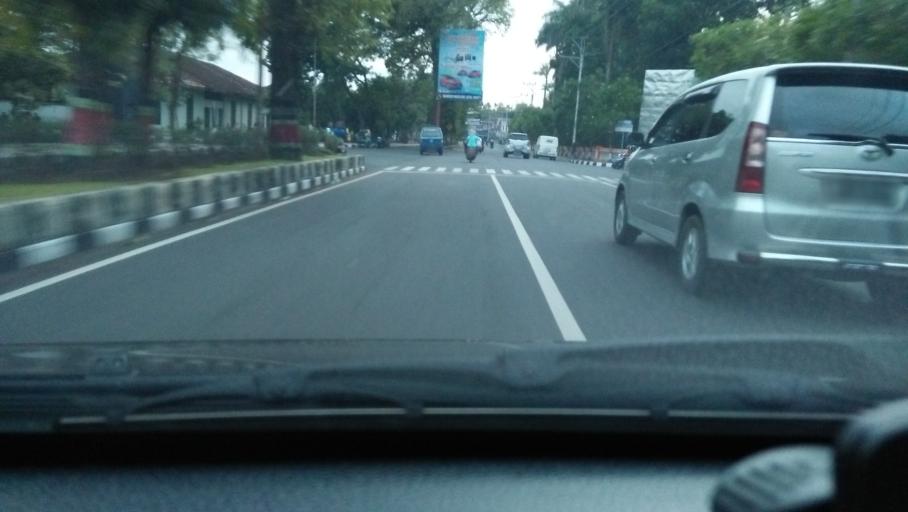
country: ID
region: Central Java
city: Magelang
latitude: -7.4682
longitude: 110.2197
